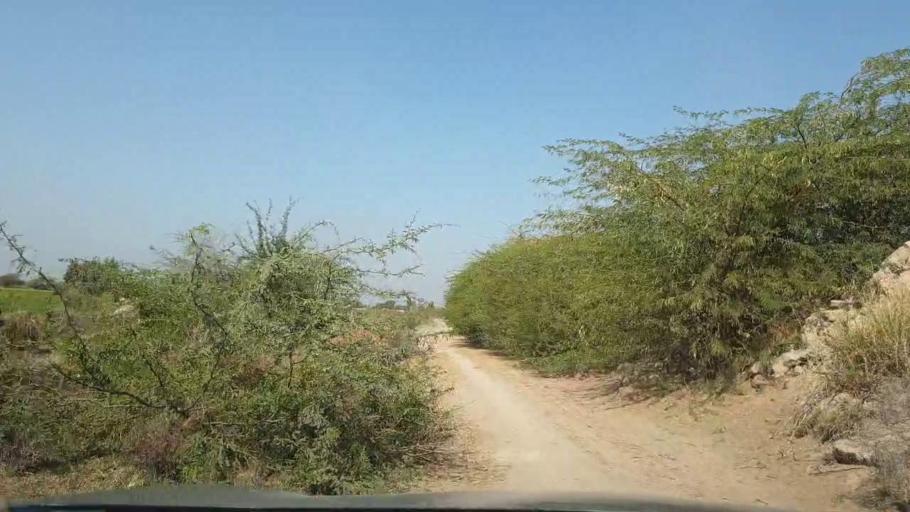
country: PK
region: Sindh
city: Berani
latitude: 25.6865
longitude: 68.8933
